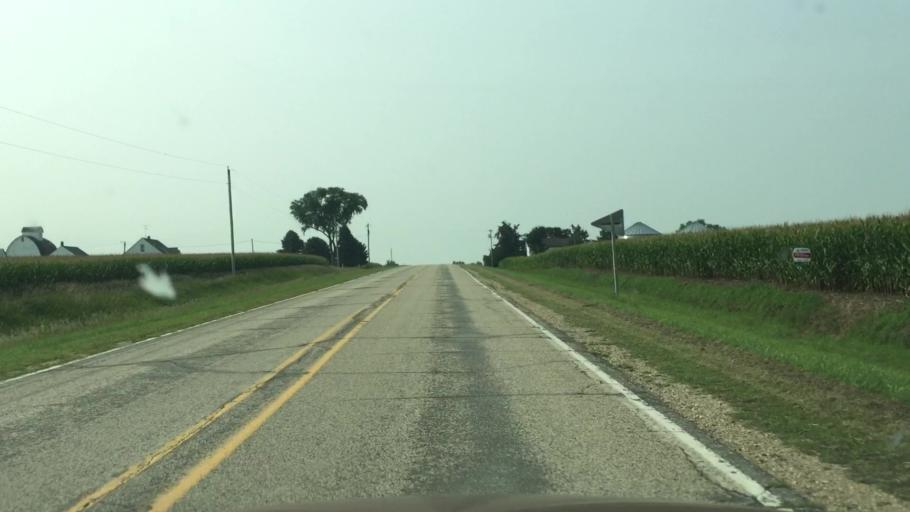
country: US
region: Iowa
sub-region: O'Brien County
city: Sheldon
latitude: 43.2716
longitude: -95.7829
